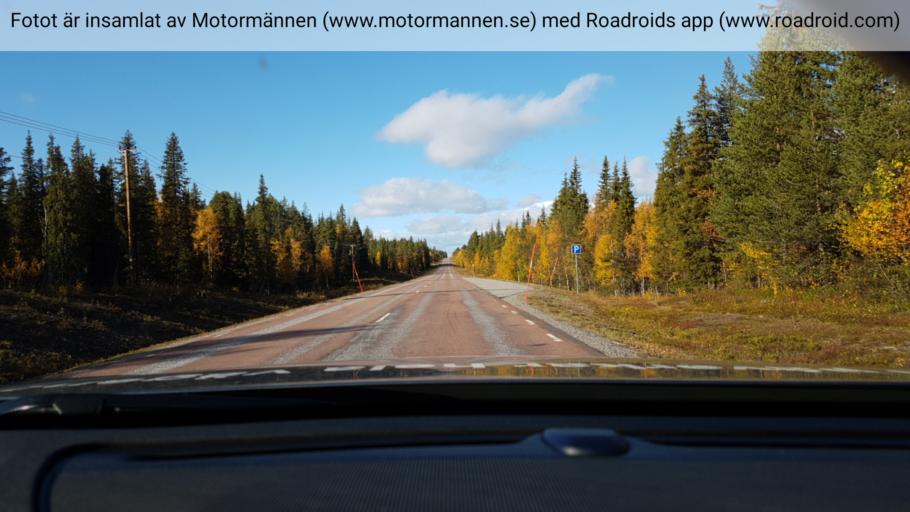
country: SE
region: Norrbotten
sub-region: Arjeplogs Kommun
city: Arjeplog
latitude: 66.0534
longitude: 18.0047
